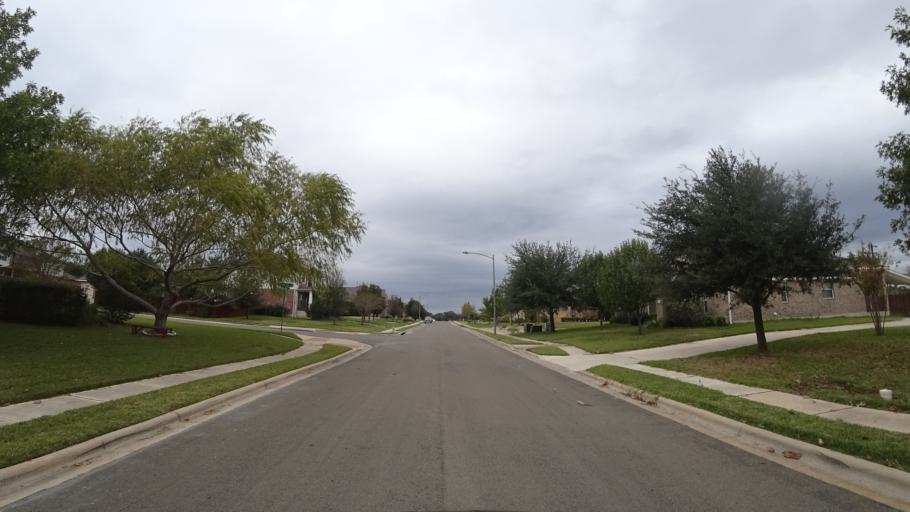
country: US
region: Texas
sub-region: Travis County
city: Shady Hollow
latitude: 30.1497
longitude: -97.8564
